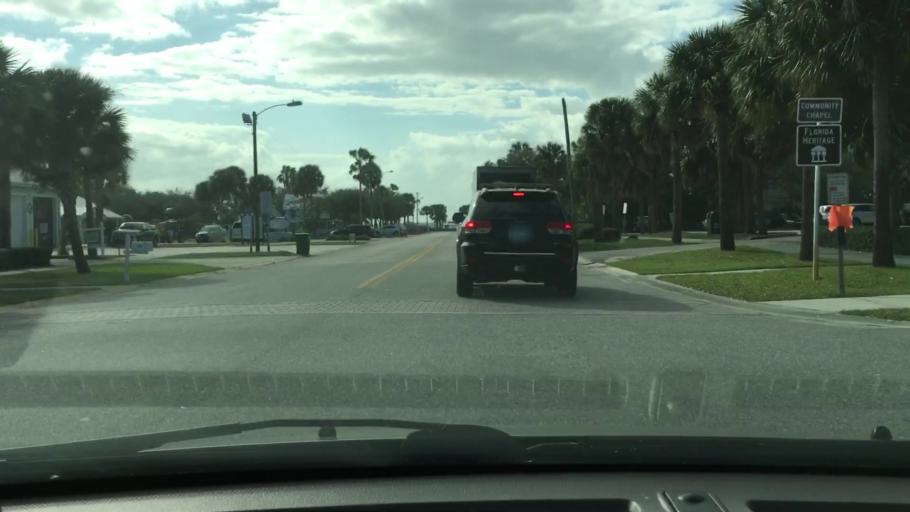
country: US
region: Florida
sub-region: Brevard County
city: Melbourne Beach
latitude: 28.0684
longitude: -80.5632
